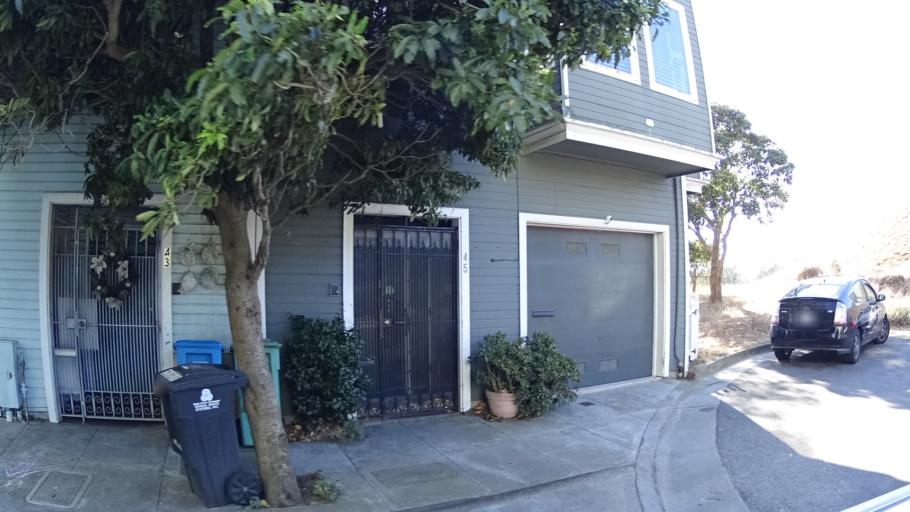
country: US
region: California
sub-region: San Mateo County
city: Brisbane
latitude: 37.7171
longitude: -122.4085
